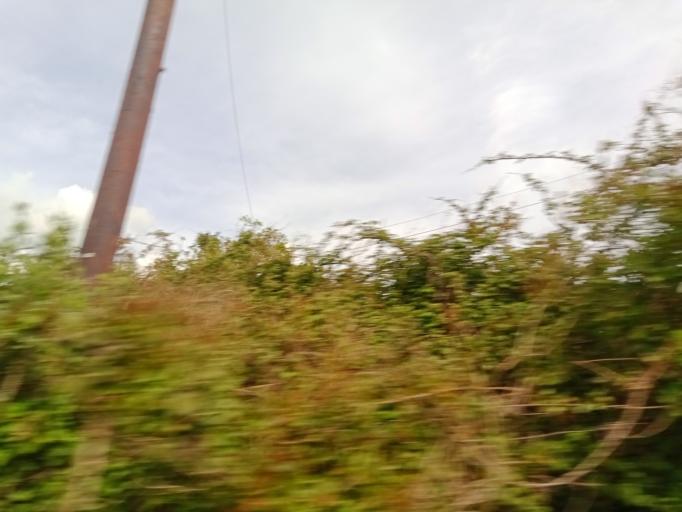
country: IE
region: Munster
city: Thurles
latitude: 52.6202
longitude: -7.7890
